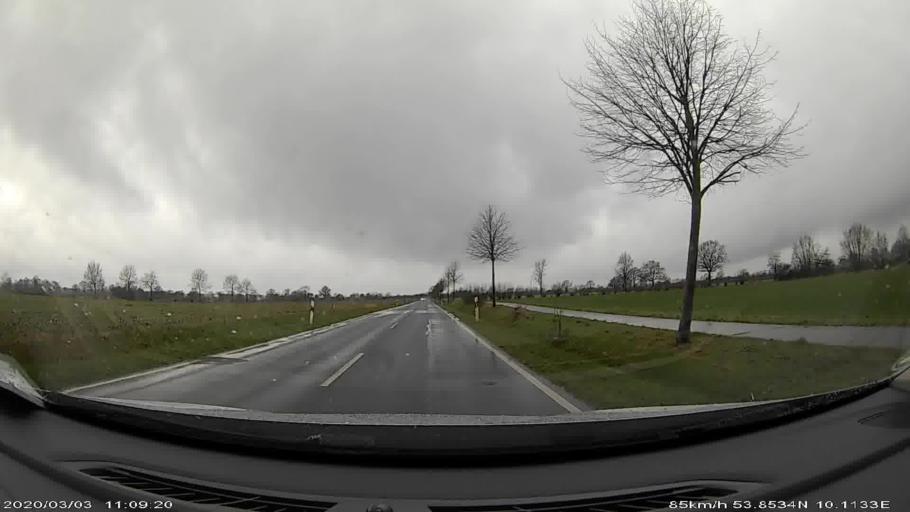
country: DE
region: Schleswig-Holstein
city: Sievershutten
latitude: 53.8553
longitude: 10.1078
